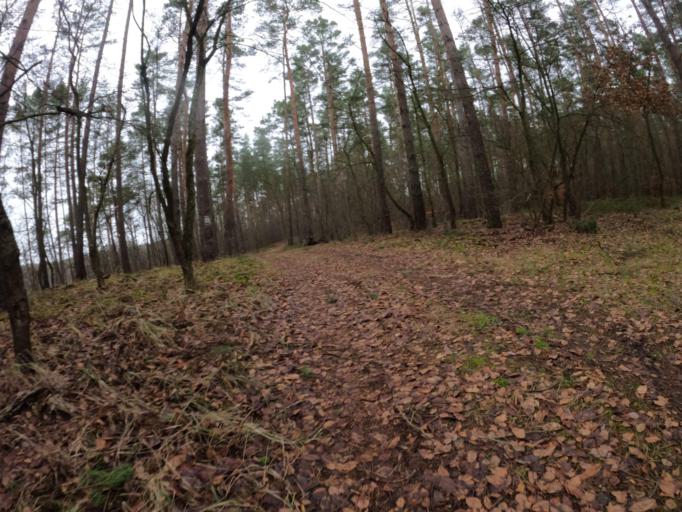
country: PL
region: West Pomeranian Voivodeship
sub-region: Powiat mysliborski
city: Debno
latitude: 52.7300
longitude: 14.7546
